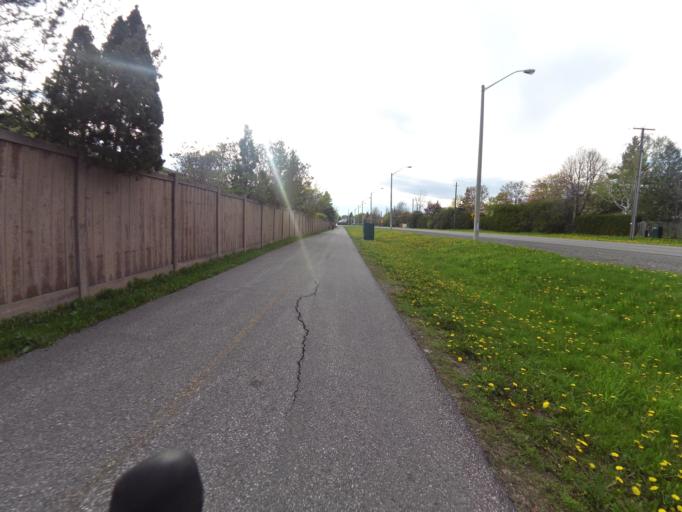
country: CA
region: Ontario
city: Bells Corners
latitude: 45.2751
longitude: -75.7688
